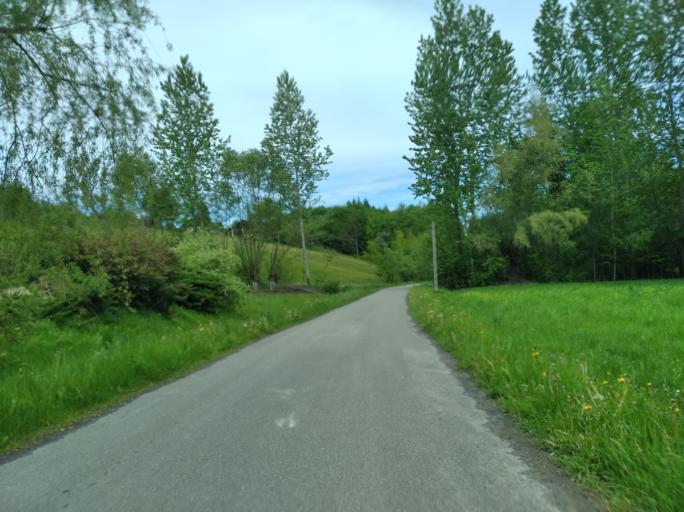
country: PL
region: Subcarpathian Voivodeship
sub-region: Powiat strzyzowski
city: Strzyzow
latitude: 49.9163
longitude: 21.7580
